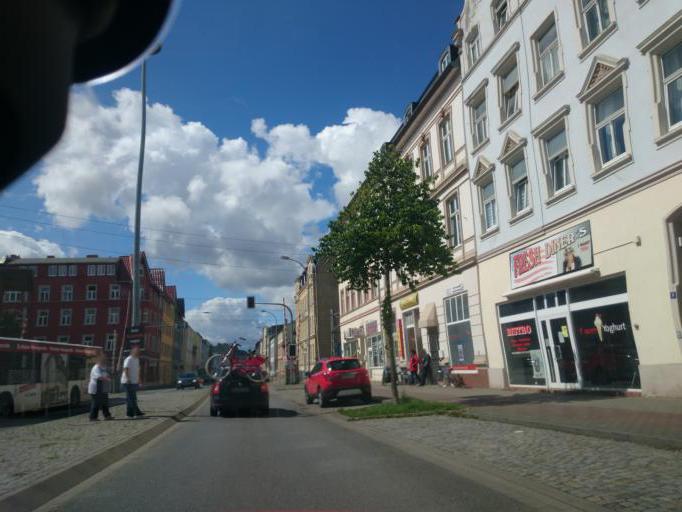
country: DE
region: Mecklenburg-Vorpommern
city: Stralsund
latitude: 54.3093
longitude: 13.0771
